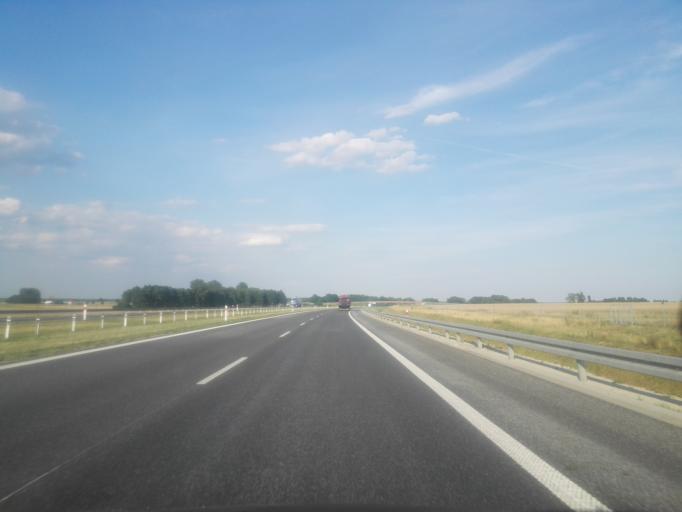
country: PL
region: Lodz Voivodeship
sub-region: Powiat wieruszowski
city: Wieruszow
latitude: 51.3369
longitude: 18.1073
